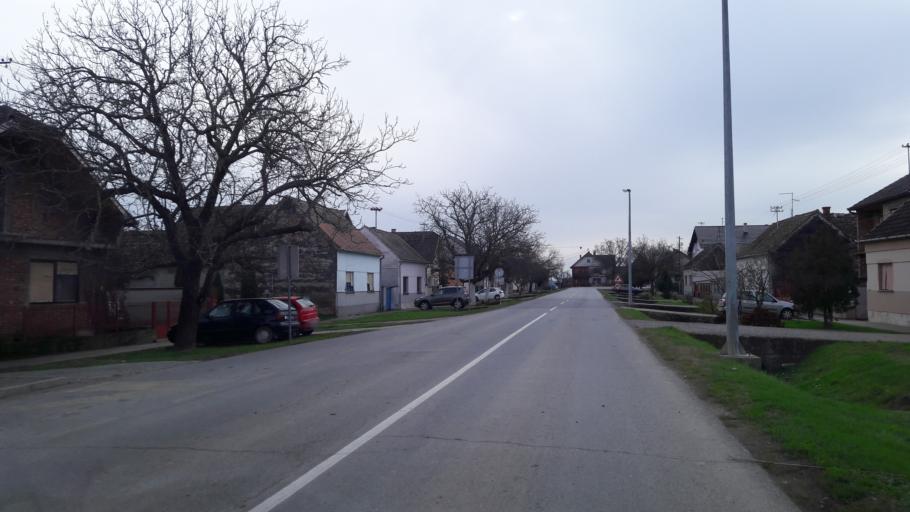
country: HR
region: Osjecko-Baranjska
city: Semeljci
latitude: 45.3838
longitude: 18.5626
